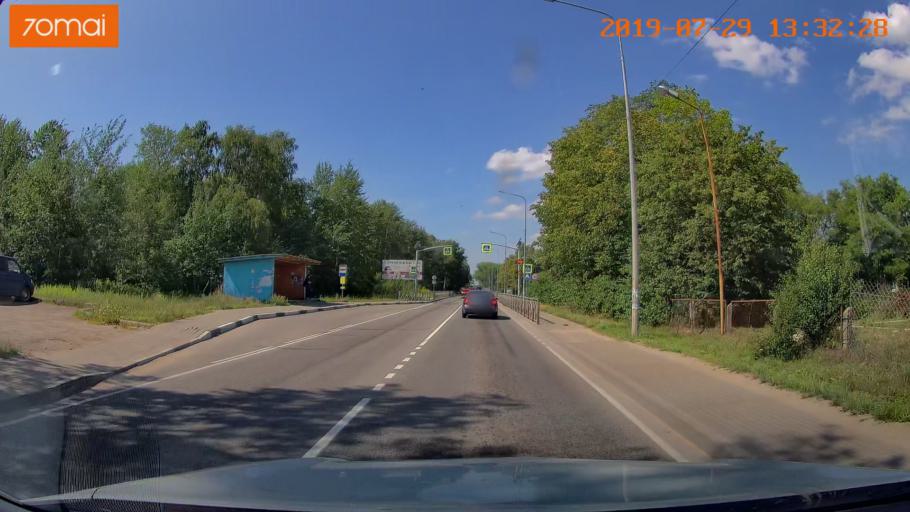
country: RU
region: Kaliningrad
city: Vzmorye
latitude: 54.6978
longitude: 20.2349
